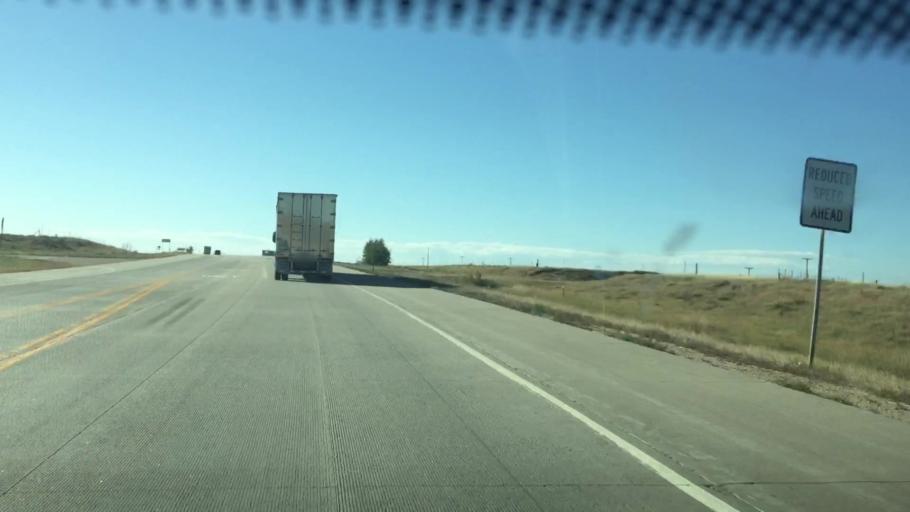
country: US
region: Colorado
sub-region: Kiowa County
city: Eads
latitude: 38.8250
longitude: -102.9961
